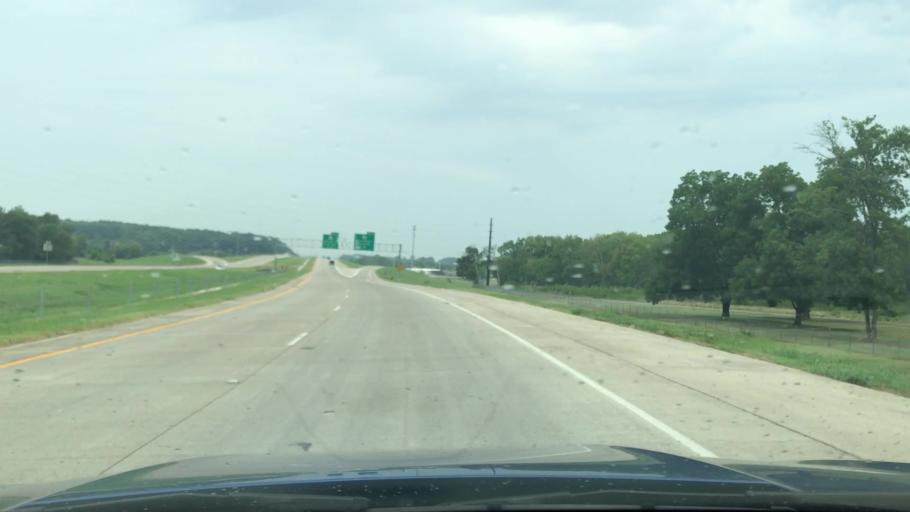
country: US
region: Louisiana
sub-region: Bossier Parish
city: Bossier City
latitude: 32.4093
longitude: -93.7179
